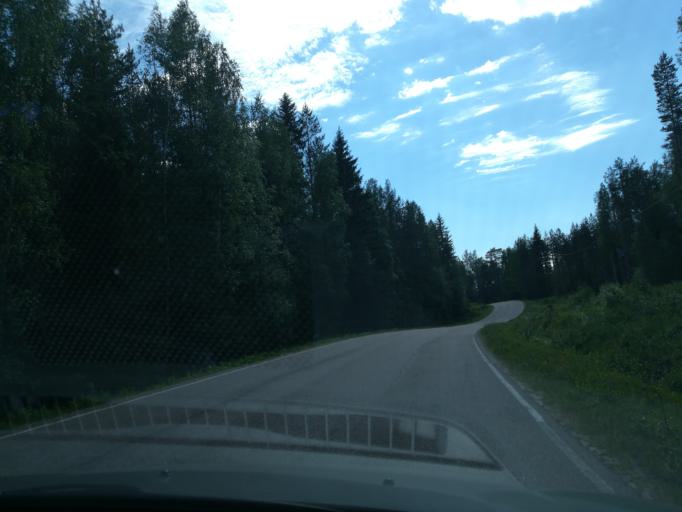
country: FI
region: South Karelia
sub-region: Imatra
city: Ruokolahti
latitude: 61.4865
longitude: 28.7880
